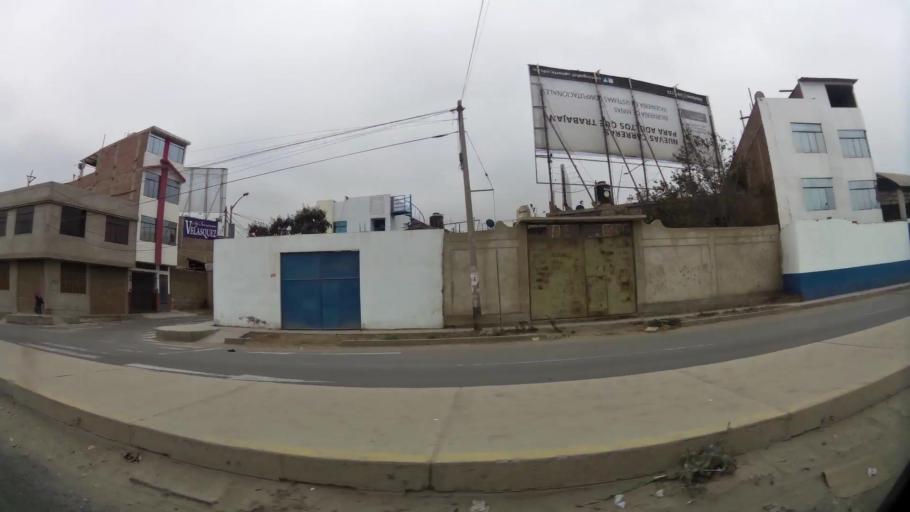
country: PE
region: La Libertad
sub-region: Provincia de Trujillo
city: La Esperanza
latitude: -8.0848
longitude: -79.0443
